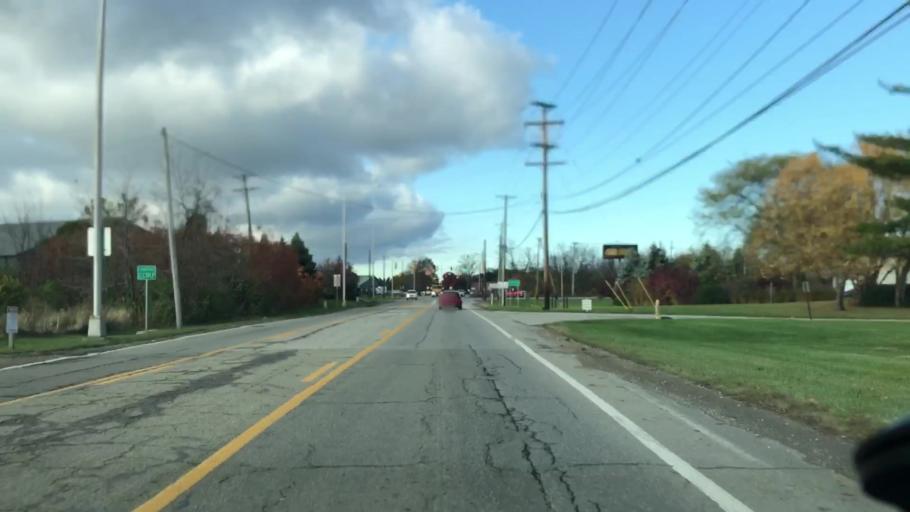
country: US
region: Ohio
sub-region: Franklin County
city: Lincoln Village
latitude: 39.9823
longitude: -83.1362
